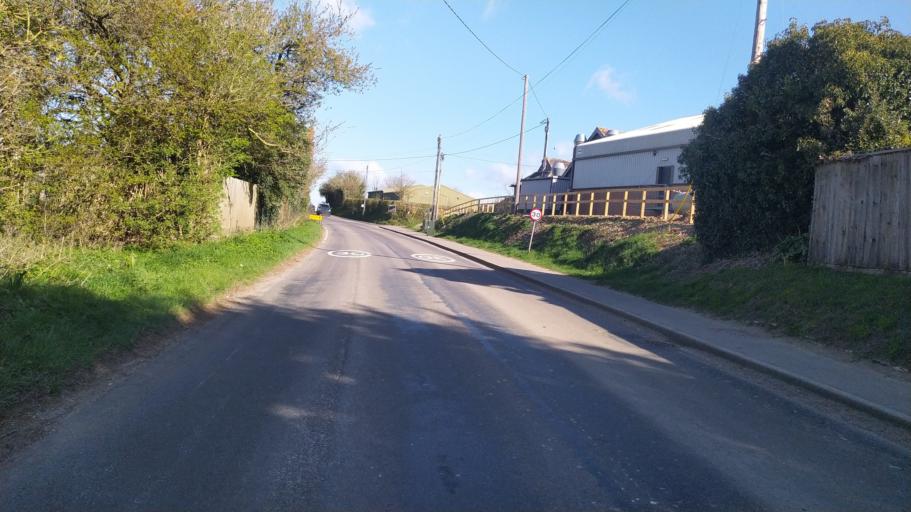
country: GB
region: England
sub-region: Dorset
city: Sturminster Newton
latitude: 50.9429
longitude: -2.3075
